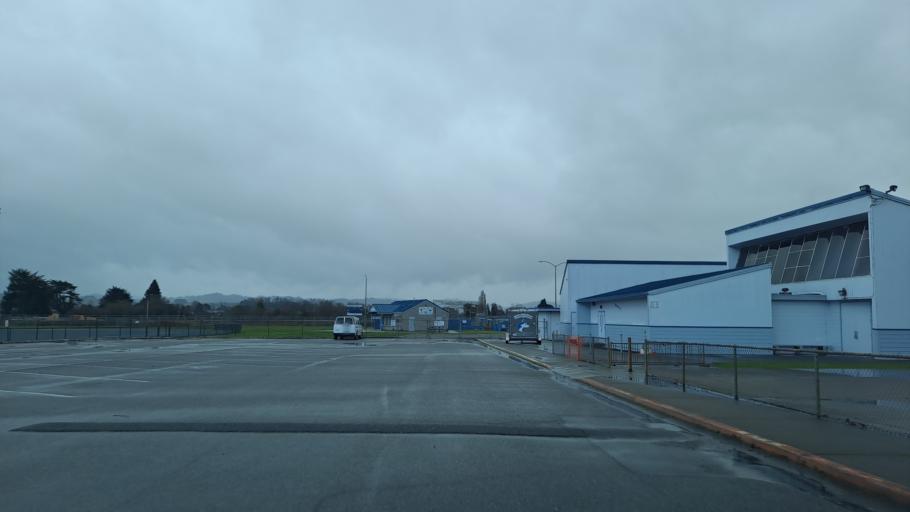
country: US
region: California
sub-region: Humboldt County
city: Fortuna
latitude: 40.5953
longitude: -124.1524
